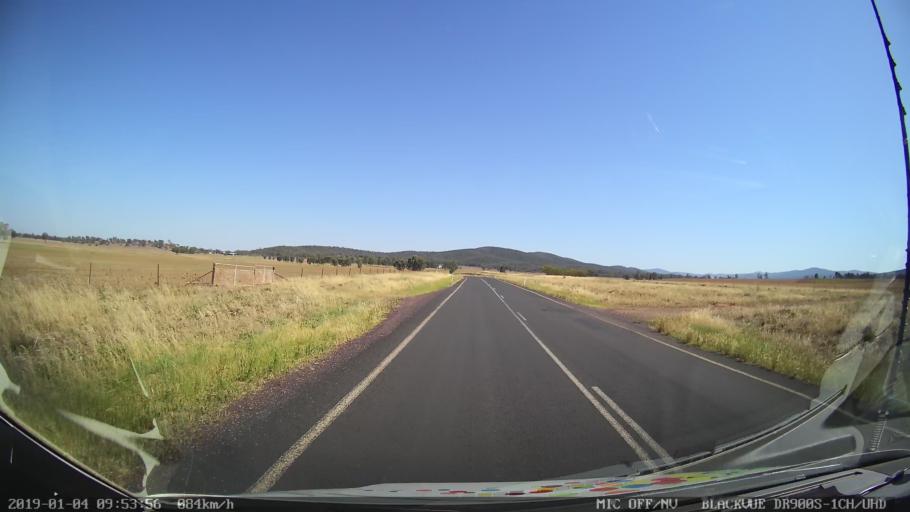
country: AU
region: New South Wales
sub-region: Cabonne
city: Canowindra
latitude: -33.5464
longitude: 148.4190
